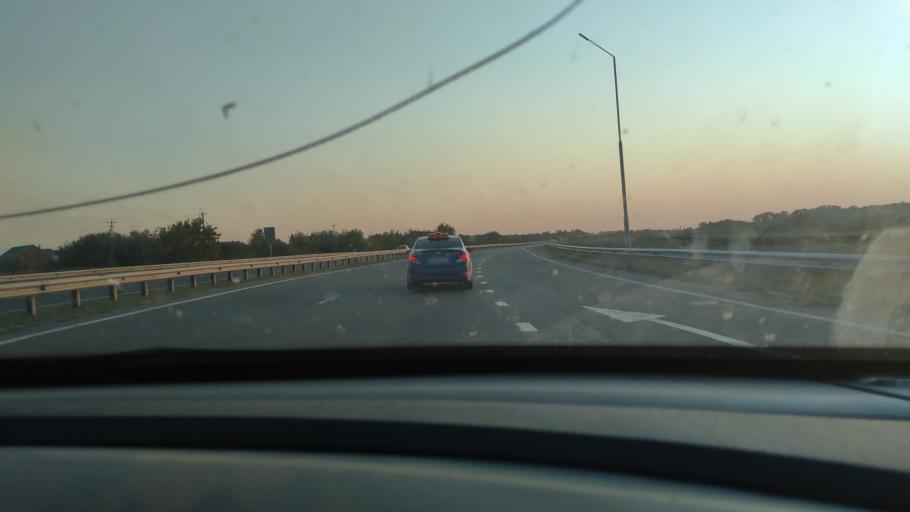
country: RU
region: Krasnodarskiy
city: Timashevsk
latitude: 45.6063
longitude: 38.9840
